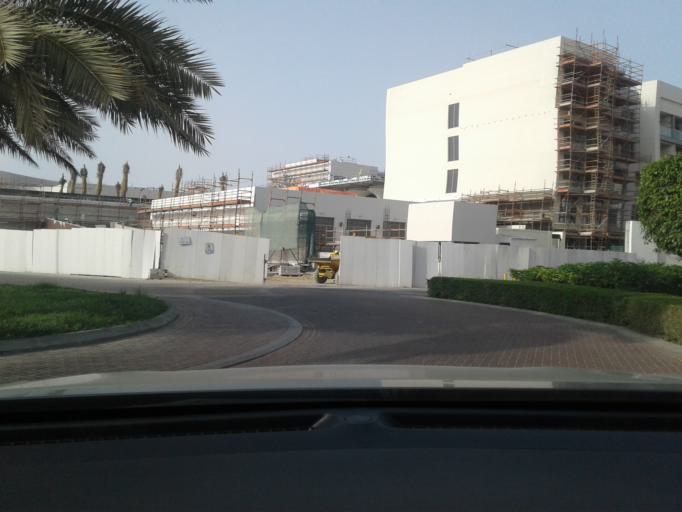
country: OM
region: Muhafazat Masqat
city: As Sib al Jadidah
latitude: 23.6266
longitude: 58.2719
